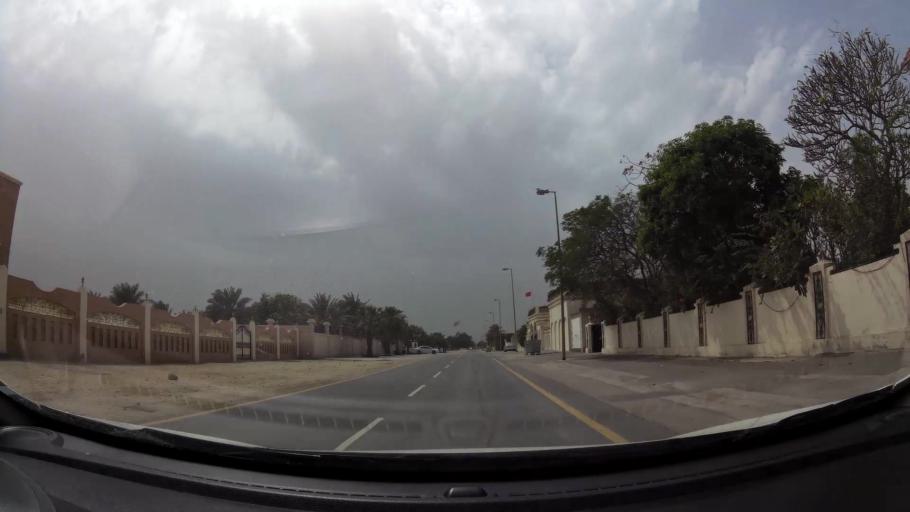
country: BH
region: Central Governorate
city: Madinat Hamad
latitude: 26.1199
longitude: 50.5314
